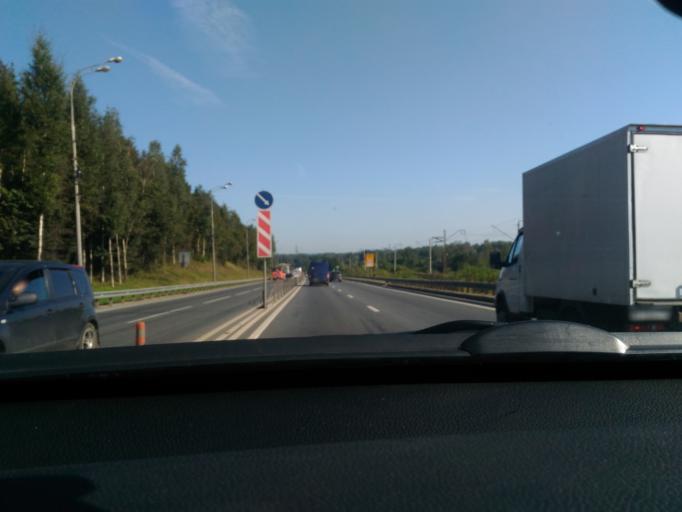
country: RU
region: Moskovskaya
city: Podosinki
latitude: 56.1942
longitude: 37.5239
